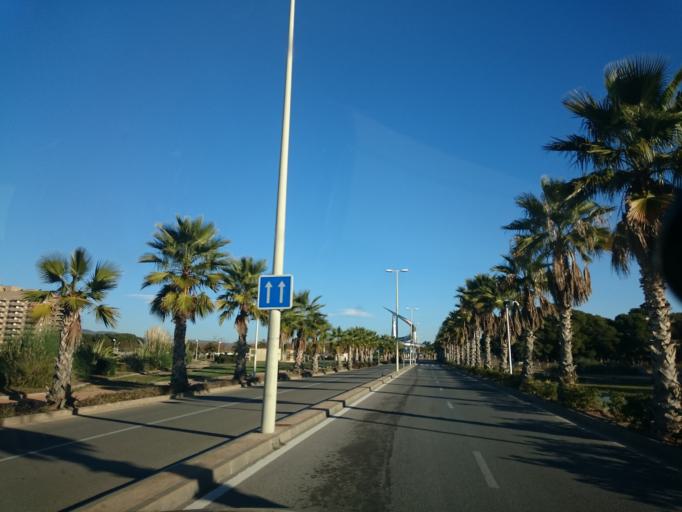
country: ES
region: Valencia
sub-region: Provincia de Castello
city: Orpesa/Oropesa del Mar
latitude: 40.1220
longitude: 0.1565
